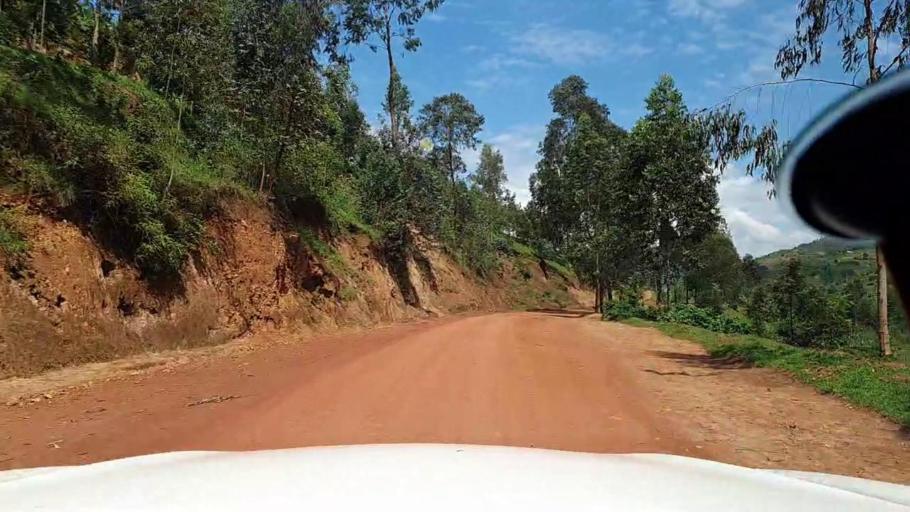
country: RW
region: Kigali
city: Kigali
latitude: -1.7834
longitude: 29.8799
